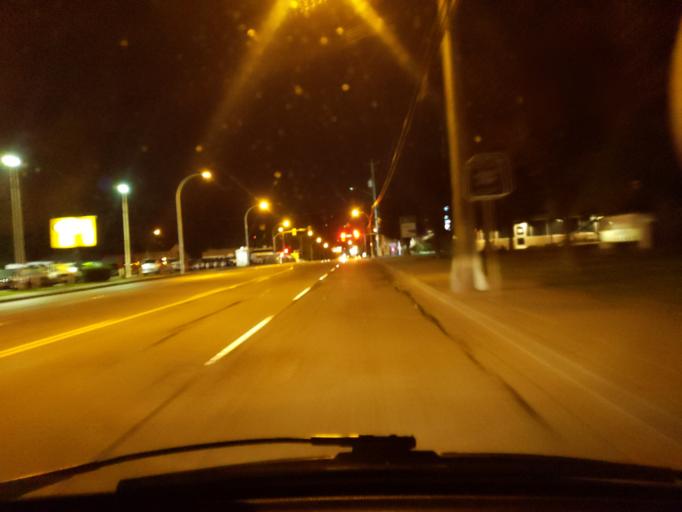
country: CA
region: British Columbia
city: Surrey
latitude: 49.1916
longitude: -122.8213
